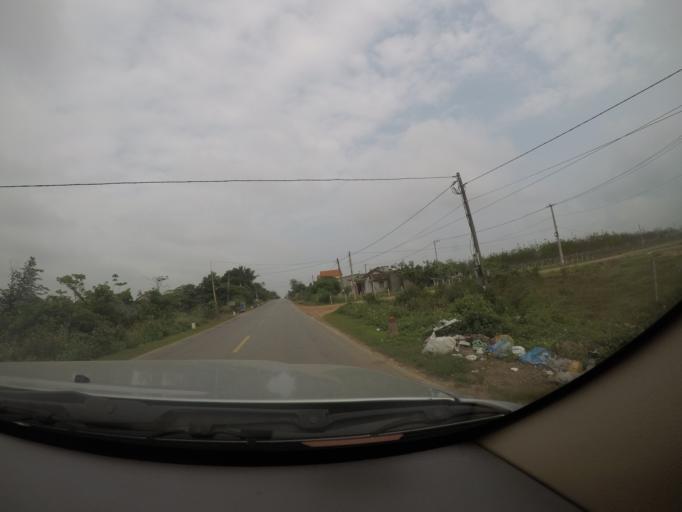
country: VN
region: Quang Binh
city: Kwang Binh
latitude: 17.4845
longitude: 106.5359
